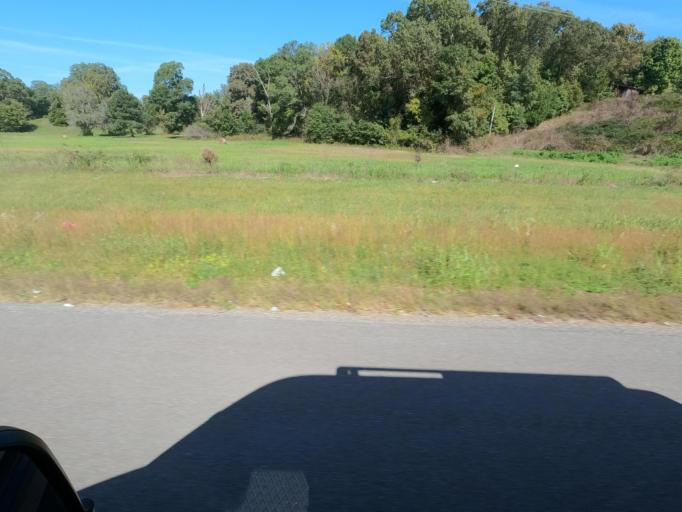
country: US
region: Tennessee
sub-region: Madison County
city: Three Way
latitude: 35.6715
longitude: -88.9455
